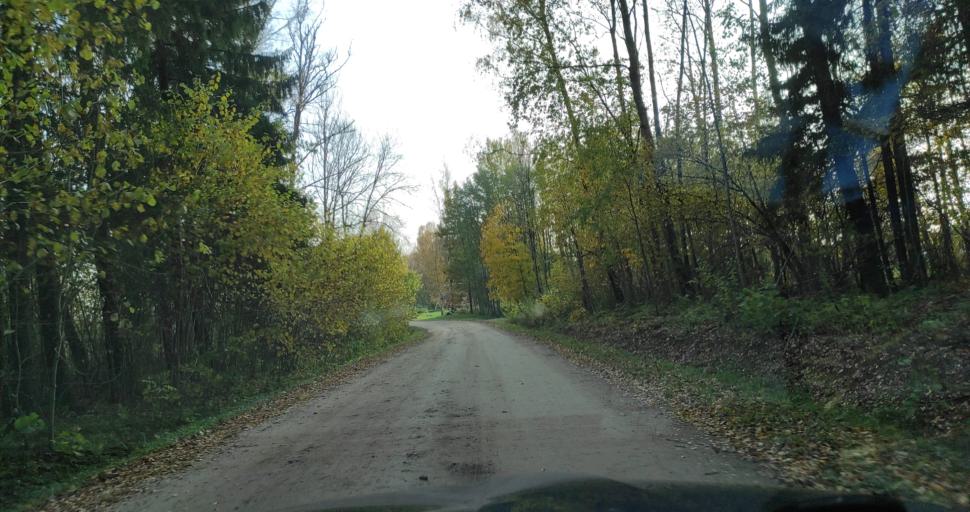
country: LV
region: Vainode
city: Vainode
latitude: 56.4262
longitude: 21.8735
